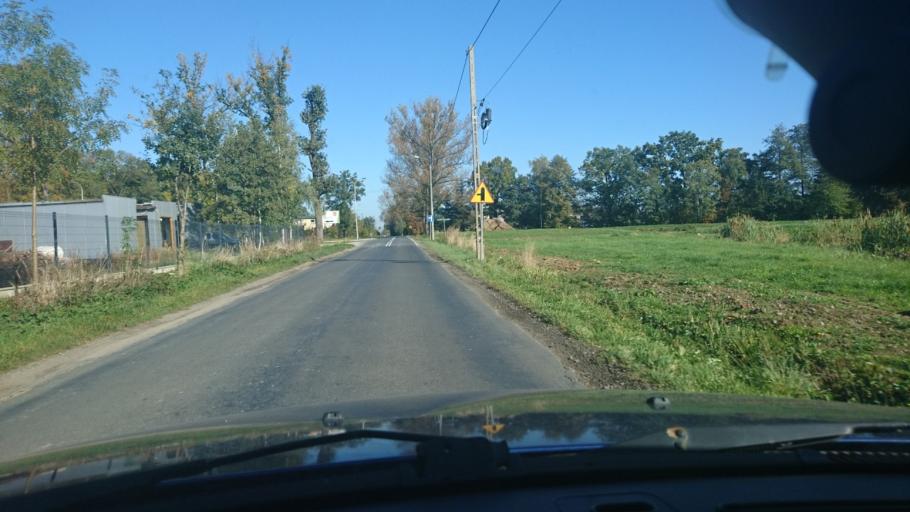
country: PL
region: Silesian Voivodeship
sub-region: Powiat bielski
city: Bronow
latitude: 49.8588
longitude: 18.9446
